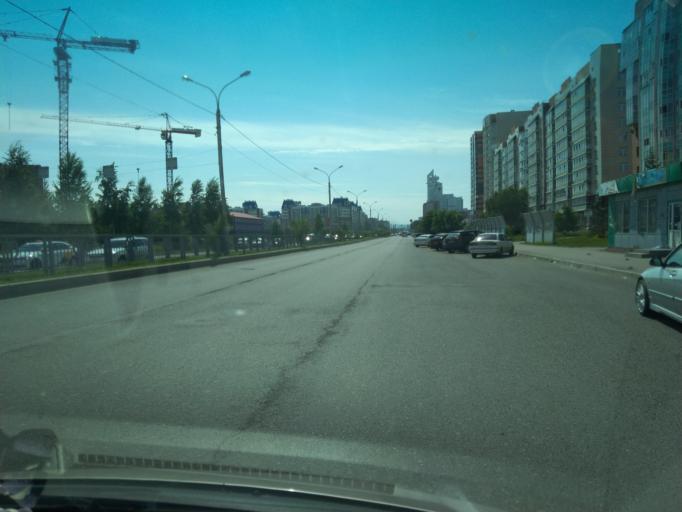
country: RU
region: Krasnoyarskiy
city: Krasnoyarsk
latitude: 56.0497
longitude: 92.9212
